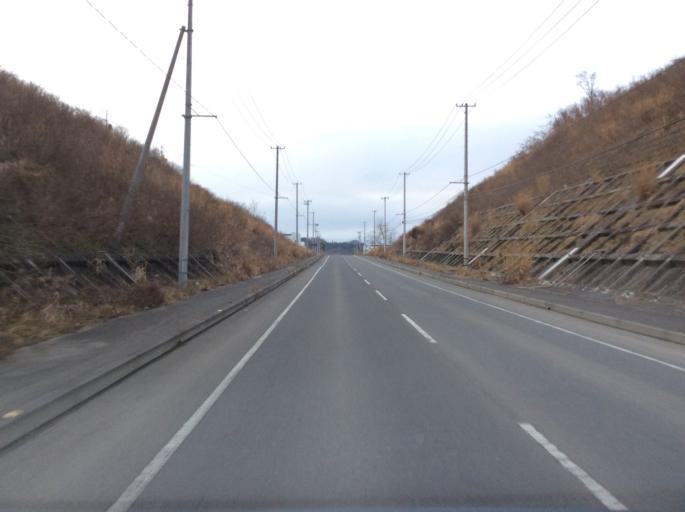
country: JP
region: Fukushima
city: Iwaki
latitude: 37.1216
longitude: 140.9788
